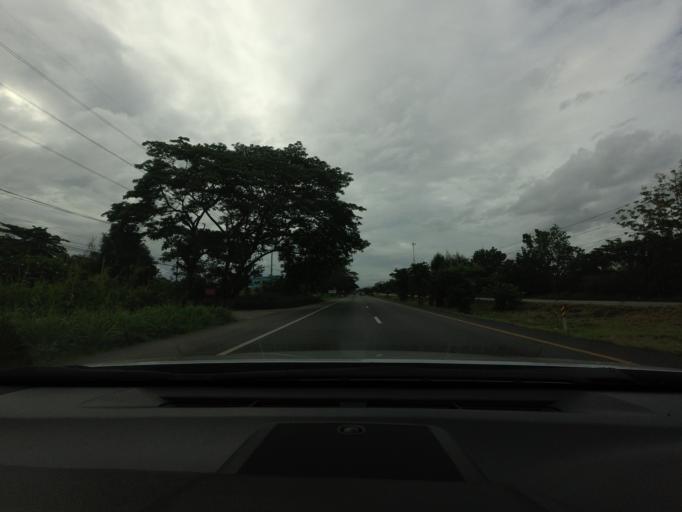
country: TH
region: Prachuap Khiri Khan
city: Hua Hin
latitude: 12.5927
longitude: 99.8638
